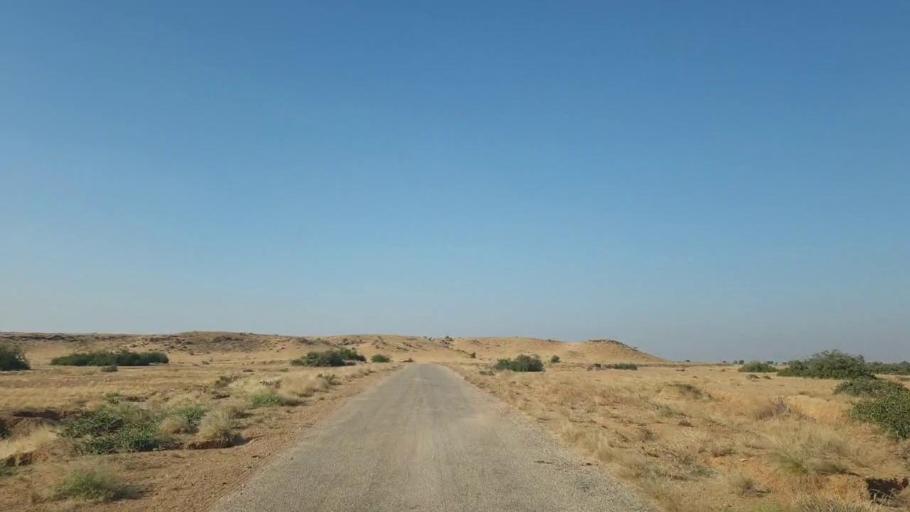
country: PK
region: Sindh
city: Malir Cantonment
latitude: 25.4129
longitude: 67.4643
